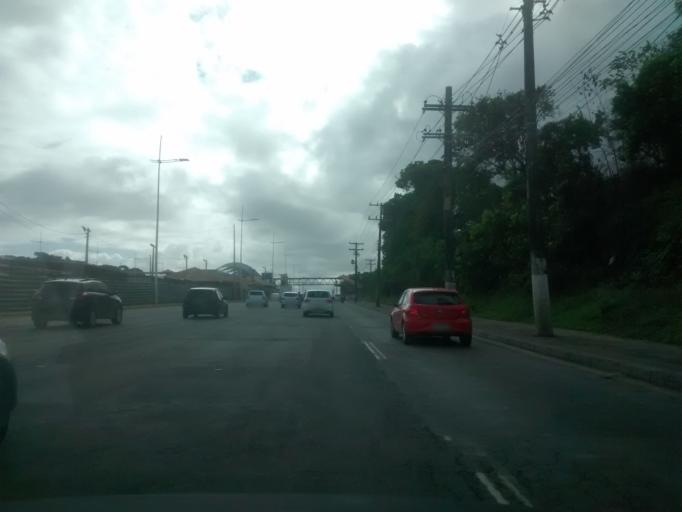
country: BR
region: Bahia
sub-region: Salvador
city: Salvador
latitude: -12.9590
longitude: -38.4309
